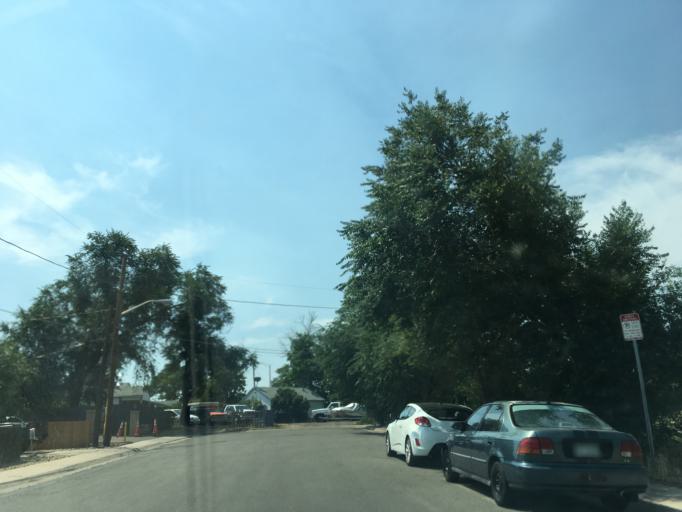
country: US
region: Colorado
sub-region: Jefferson County
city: Lakewood
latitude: 39.6989
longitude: -105.0485
